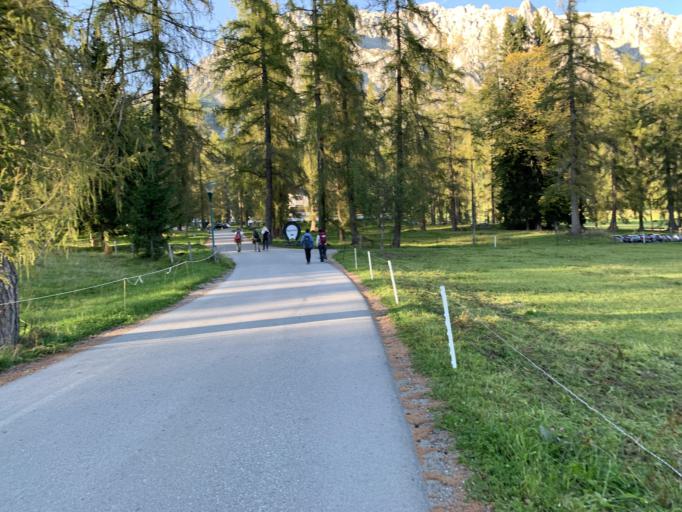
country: AT
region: Styria
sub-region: Politischer Bezirk Liezen
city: Schladming
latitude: 47.4247
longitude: 13.6441
